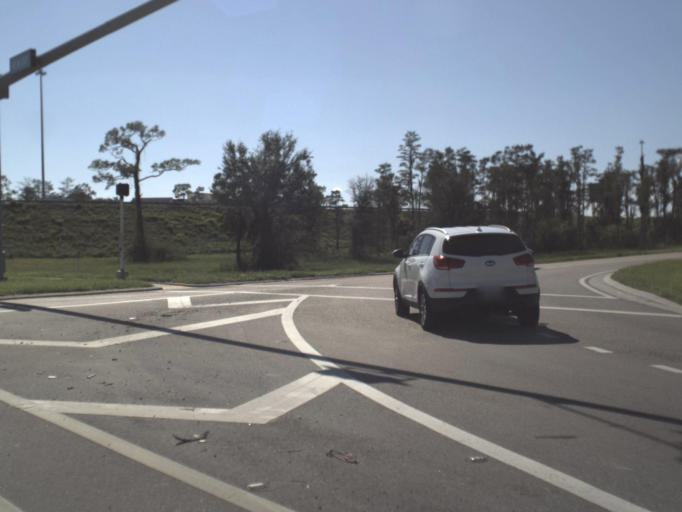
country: US
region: Florida
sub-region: Lee County
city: Fort Myers
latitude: 26.6353
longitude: -81.8044
